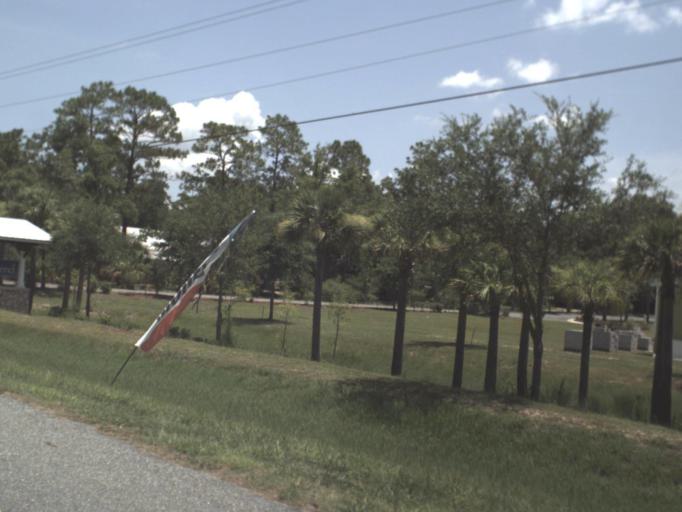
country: US
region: Florida
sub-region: Taylor County
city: Steinhatchee
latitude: 29.6914
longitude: -83.3561
